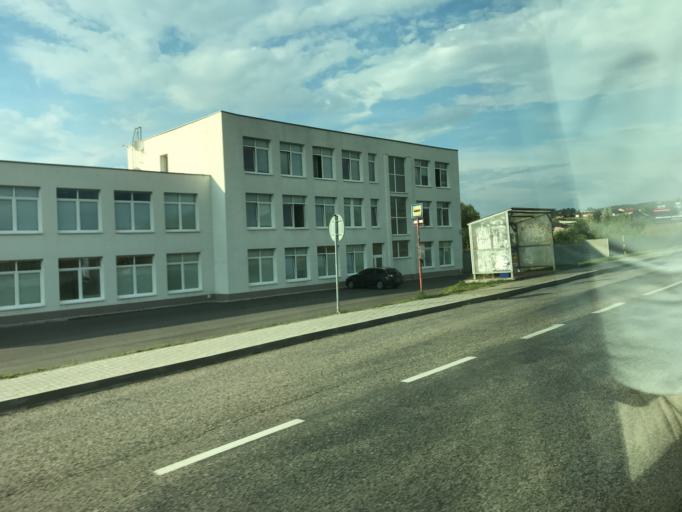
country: CZ
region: Jihocesky
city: Rudolfov
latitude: 48.9863
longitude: 14.5197
